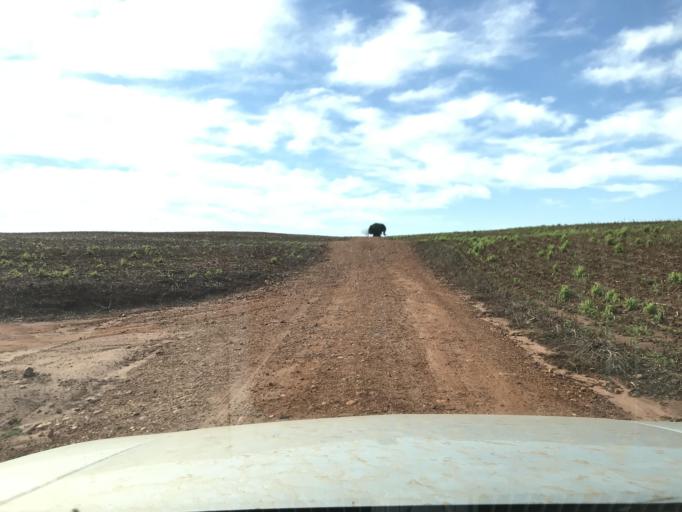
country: BR
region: Parana
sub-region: Palotina
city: Palotina
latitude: -24.1857
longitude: -53.8359
